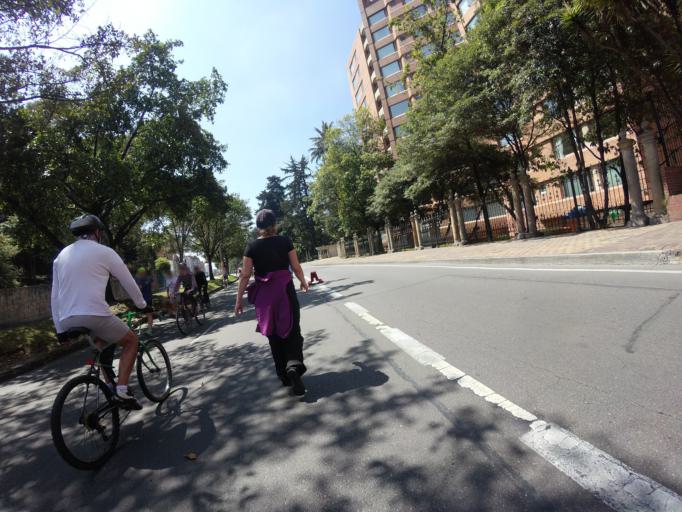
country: CO
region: Bogota D.C.
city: Barrio San Luis
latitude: 4.6737
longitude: -74.0426
